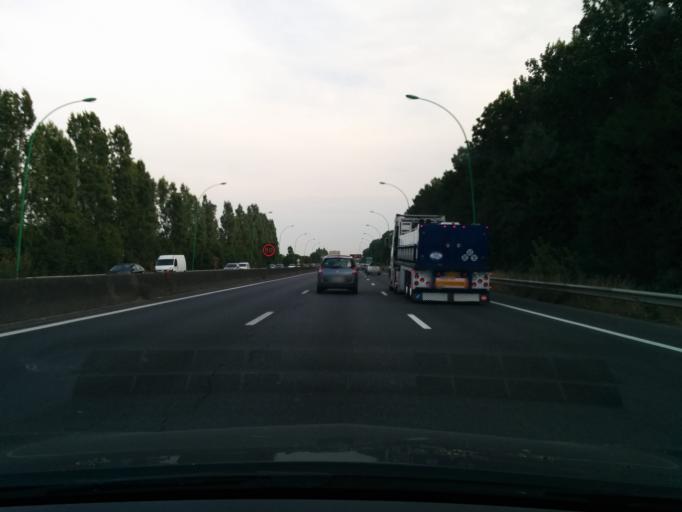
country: FR
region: Midi-Pyrenees
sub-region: Departement de la Haute-Garonne
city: Balma
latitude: 43.6212
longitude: 1.4814
